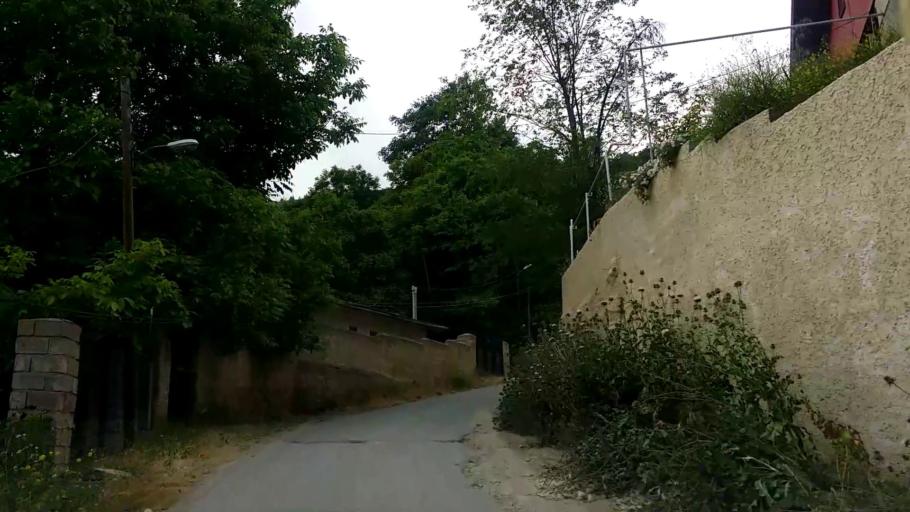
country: IR
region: Mazandaran
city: Chalus
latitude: 36.5556
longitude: 51.2733
